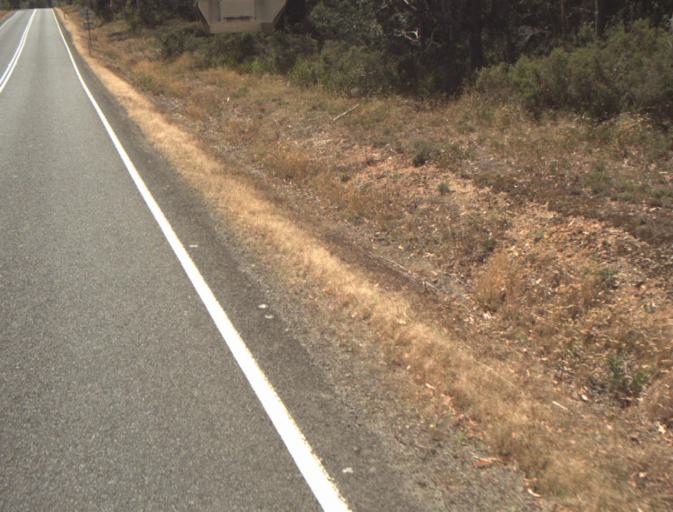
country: AU
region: Tasmania
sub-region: Dorset
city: Scottsdale
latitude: -41.3050
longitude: 147.3817
